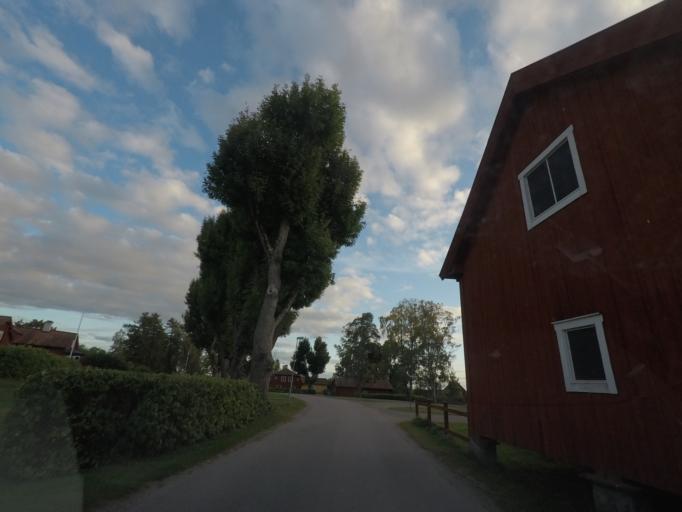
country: SE
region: Vaestmanland
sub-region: Hallstahammars Kommun
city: Kolback
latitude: 59.5239
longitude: 16.2486
